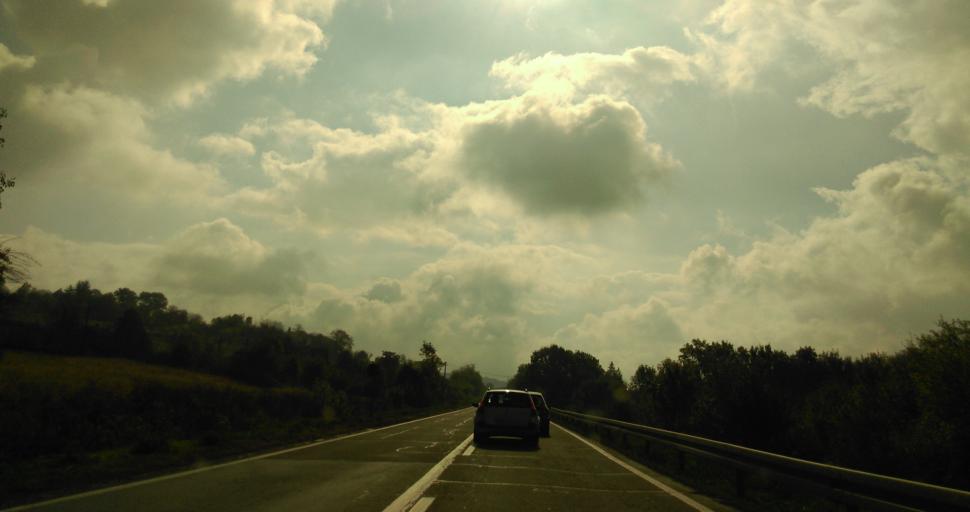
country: RS
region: Central Serbia
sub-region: Kolubarski Okrug
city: Ljig
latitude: 44.2905
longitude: 20.2666
